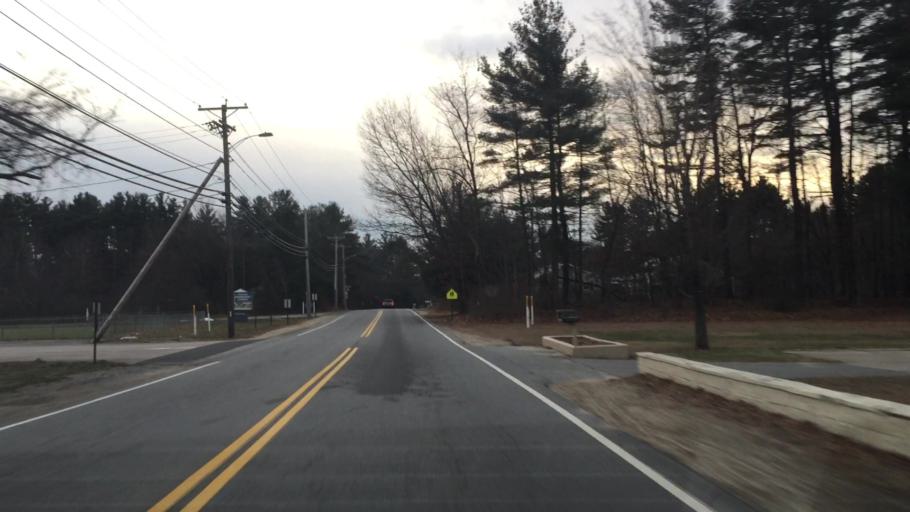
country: US
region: New Hampshire
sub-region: Hillsborough County
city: Pelham
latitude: 42.7278
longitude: -71.3280
